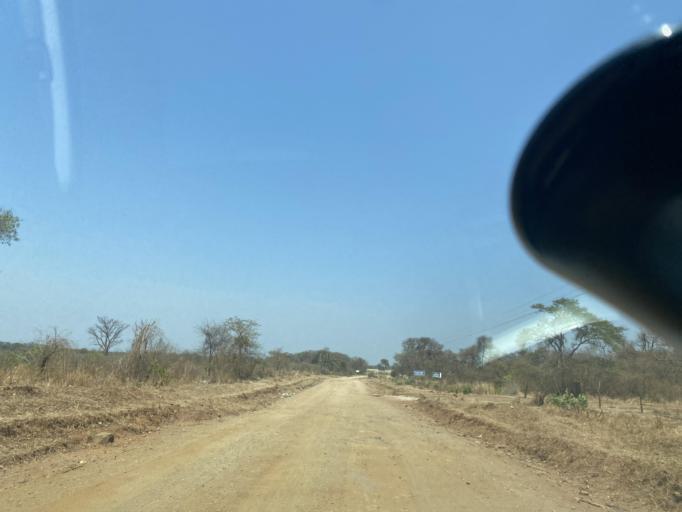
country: ZM
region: Lusaka
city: Lusaka
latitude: -15.5330
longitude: 28.0936
